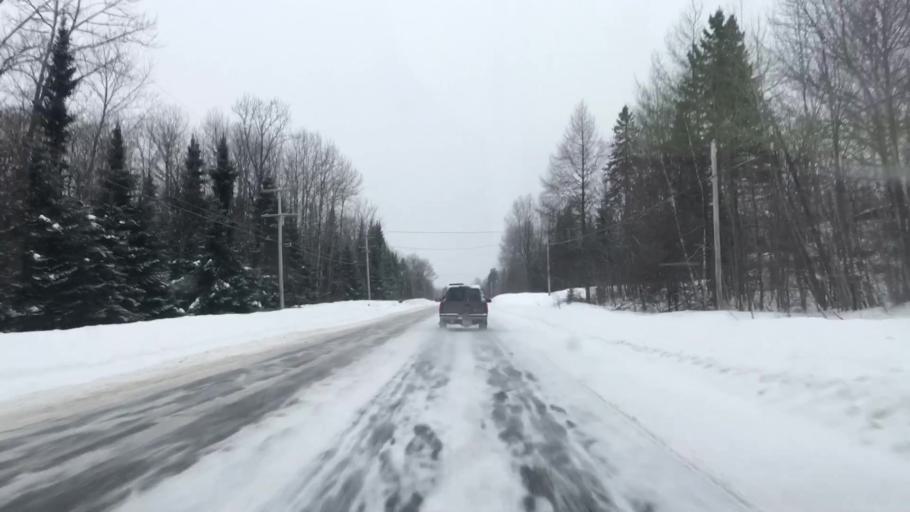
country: US
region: Maine
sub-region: Penobscot County
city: Medway
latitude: 45.5869
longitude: -68.4351
